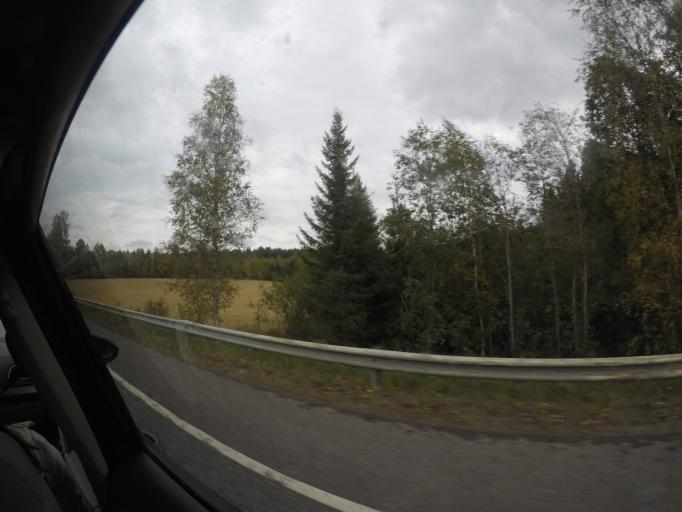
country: FI
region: Haeme
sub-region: Haemeenlinna
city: Parola
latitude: 61.1787
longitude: 24.4127
